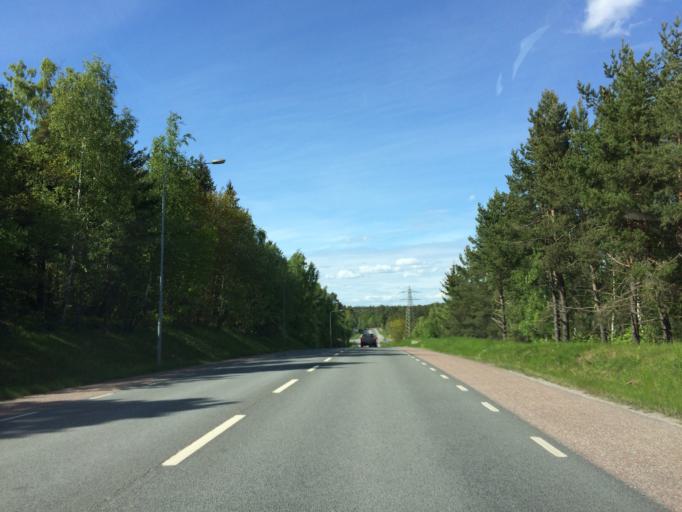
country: SE
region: Stockholm
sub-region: Sollentuna Kommun
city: Sollentuna
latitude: 59.4305
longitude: 17.9943
